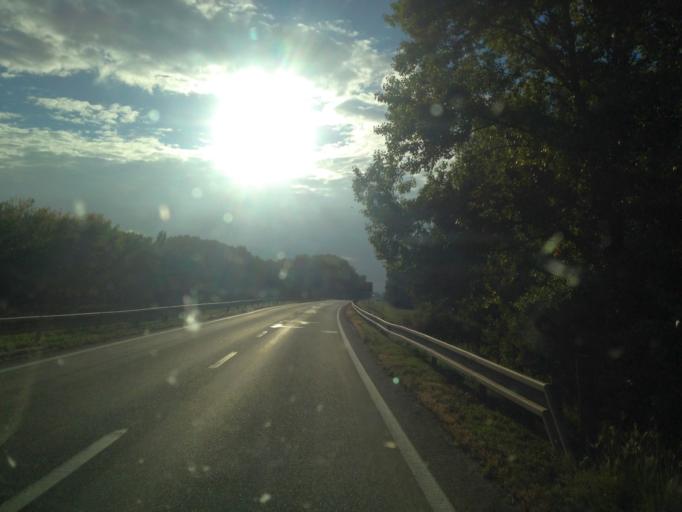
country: HU
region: Komarom-Esztergom
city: Dunaalmas
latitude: 47.7415
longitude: 18.3195
